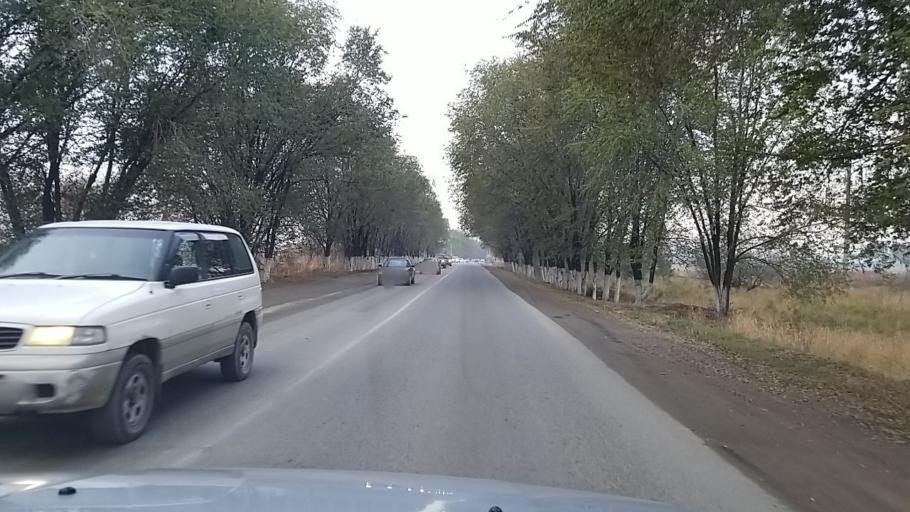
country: KZ
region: Almaty Oblysy
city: Burunday
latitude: 43.3559
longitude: 76.7984
